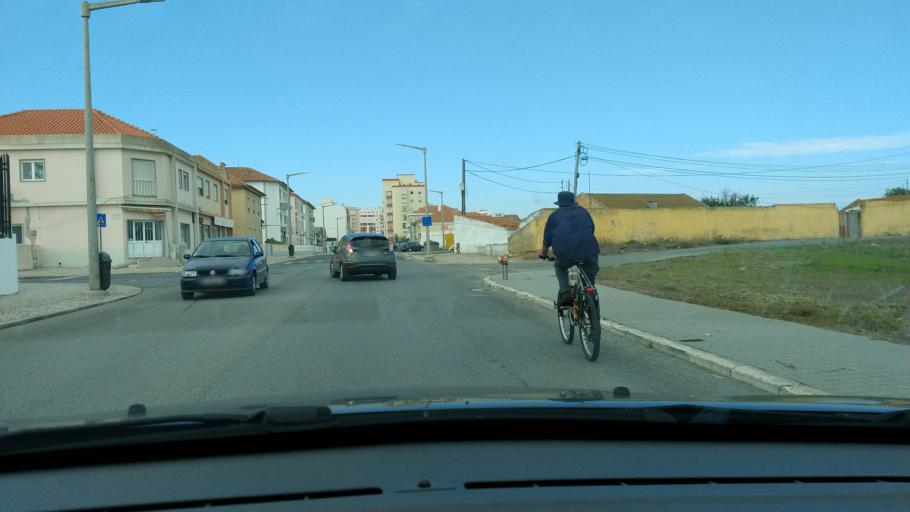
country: PT
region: Leiria
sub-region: Peniche
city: Peniche
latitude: 39.3610
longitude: -9.3850
